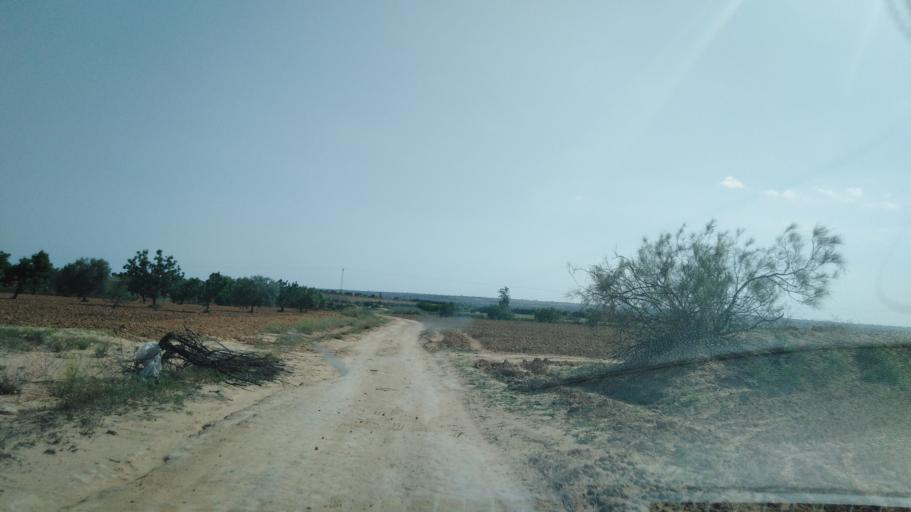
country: TN
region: Safaqis
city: Bi'r `Ali Bin Khalifah
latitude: 34.7920
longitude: 10.3716
